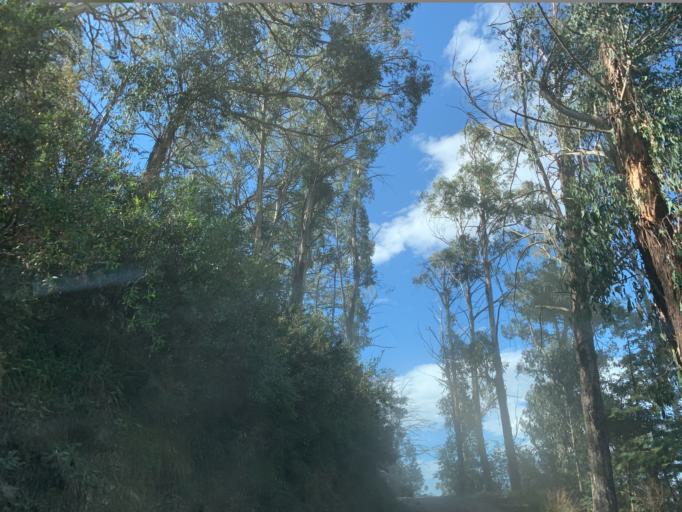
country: AU
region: Victoria
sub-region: Mansfield
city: Mansfield
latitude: -37.1004
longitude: 146.4989
